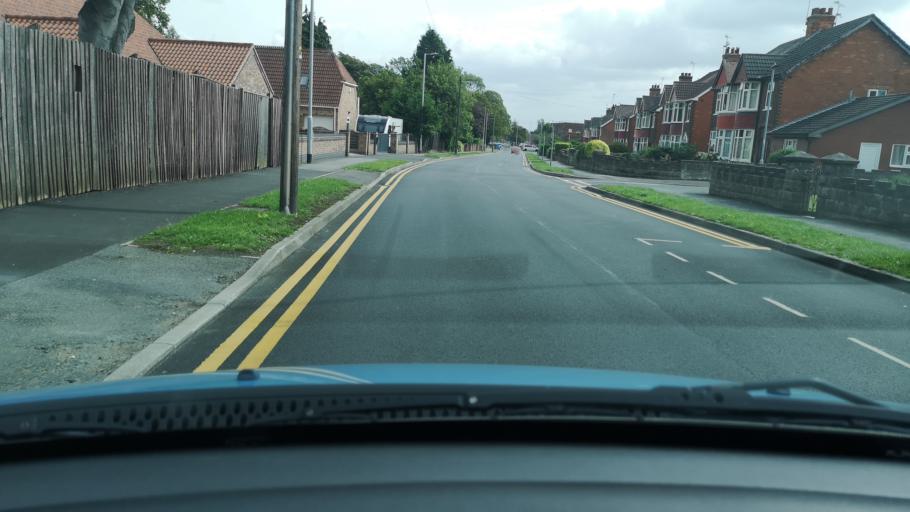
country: GB
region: England
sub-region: North Lincolnshire
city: Scunthorpe
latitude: 53.5863
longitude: -0.6587
